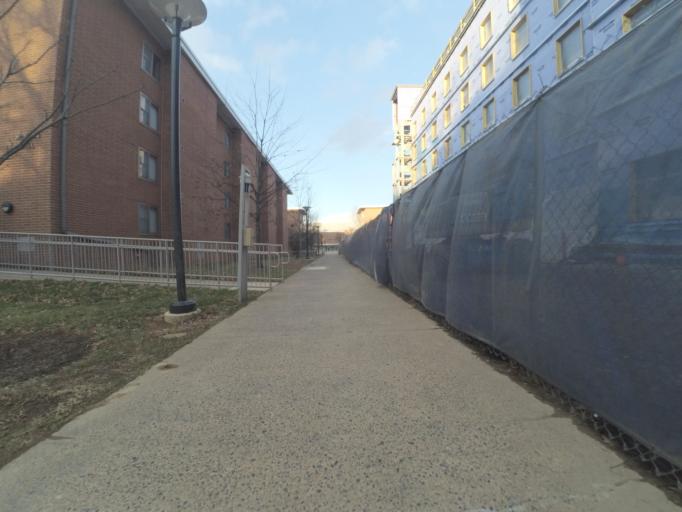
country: US
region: Pennsylvania
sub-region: Centre County
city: State College
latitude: 40.8018
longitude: -77.8669
